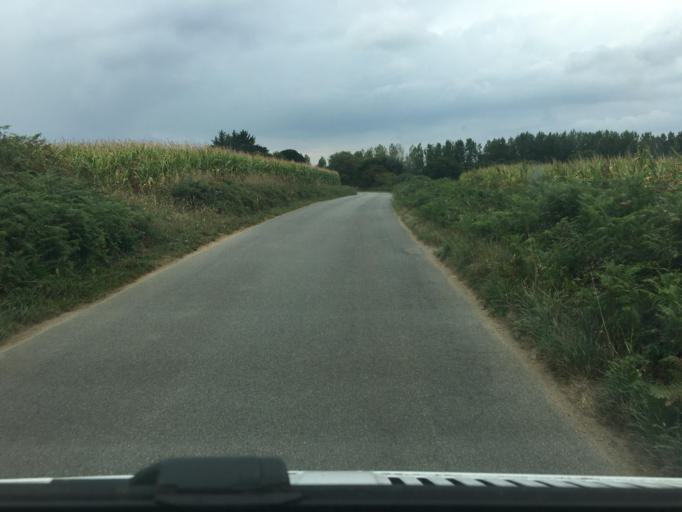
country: FR
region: Brittany
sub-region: Departement du Finistere
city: Beuzec-Cap-Sizun
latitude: 48.0768
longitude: -4.4759
